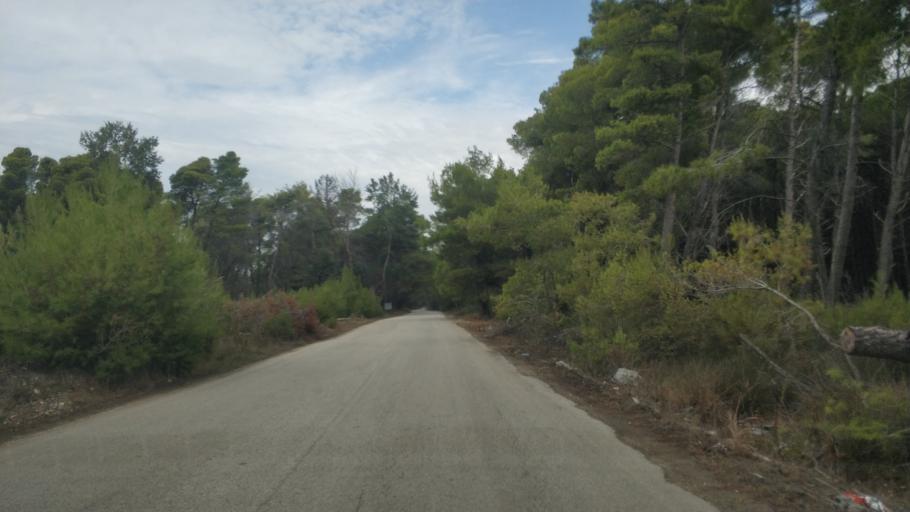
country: AL
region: Vlore
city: Vlore
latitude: 40.4813
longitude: 19.4491
